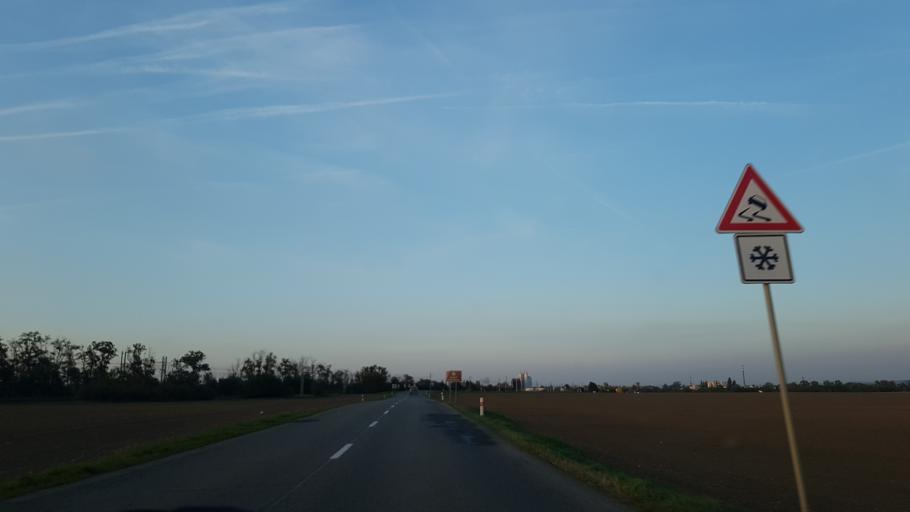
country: CZ
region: Zlin
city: Zlechov
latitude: 49.0564
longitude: 17.4032
